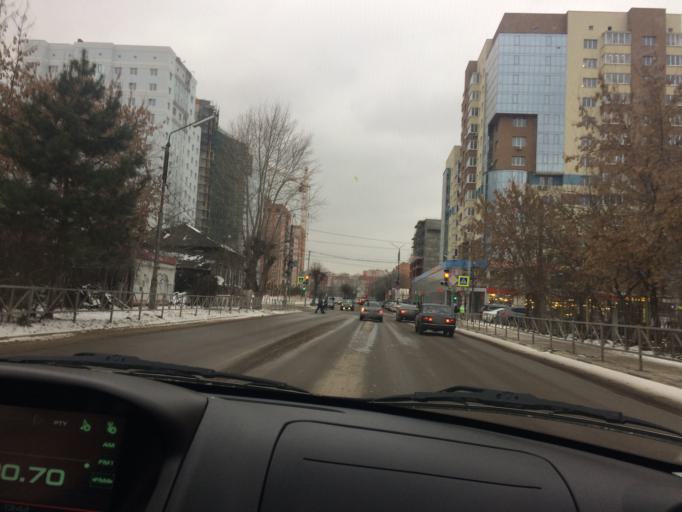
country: RU
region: Rjazan
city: Ryazan'
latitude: 54.6235
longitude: 39.7354
